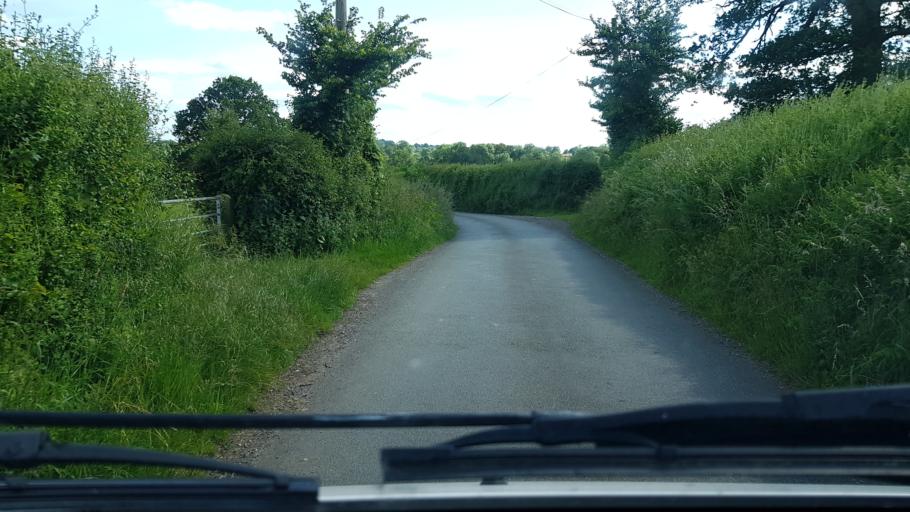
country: GB
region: England
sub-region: Shropshire
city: Romsley
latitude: 52.4440
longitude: -2.3005
